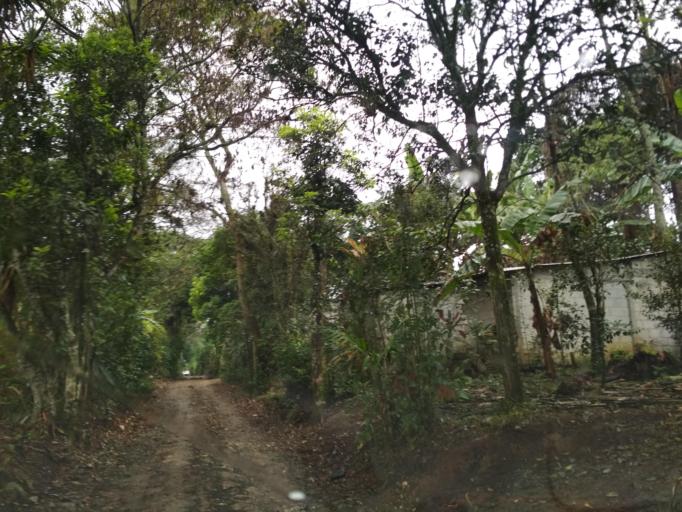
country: MX
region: Veracruz
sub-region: Amatlan de los Reyes
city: Centro de Readaptacion Social
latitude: 18.8345
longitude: -96.9354
